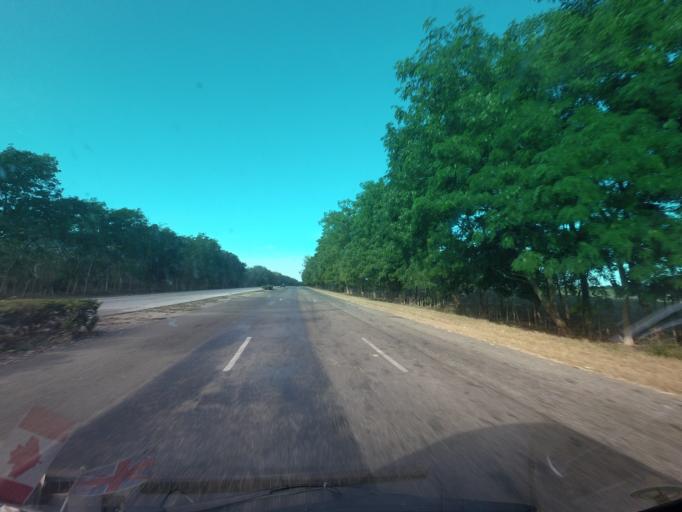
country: CU
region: Cienfuegos
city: Rodas
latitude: 22.4412
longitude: -80.5132
